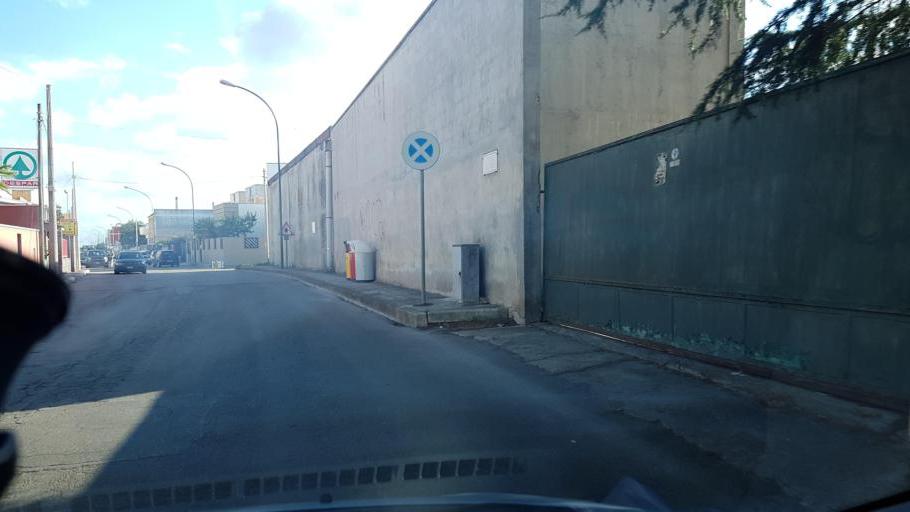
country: IT
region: Apulia
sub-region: Provincia di Lecce
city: Squinzano
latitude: 40.4317
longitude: 18.0316
